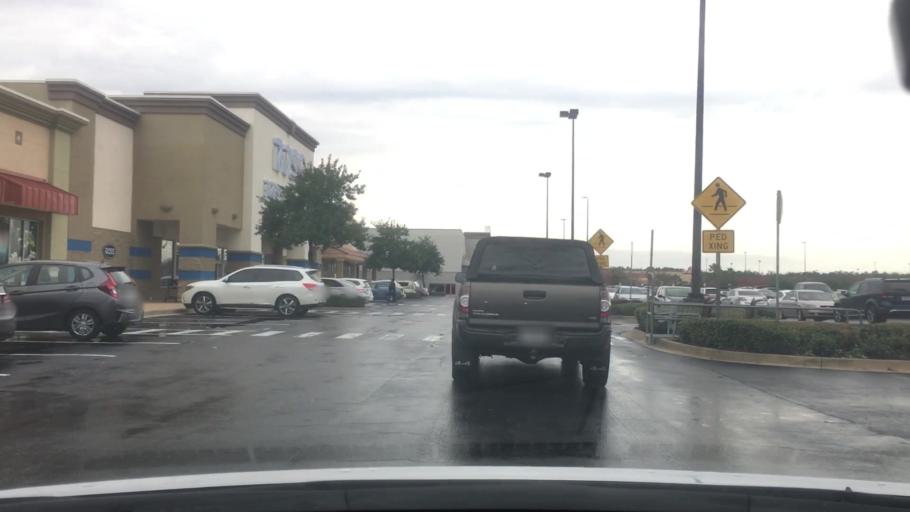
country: US
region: Florida
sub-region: Duval County
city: Atlantic Beach
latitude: 30.3178
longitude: -81.4900
